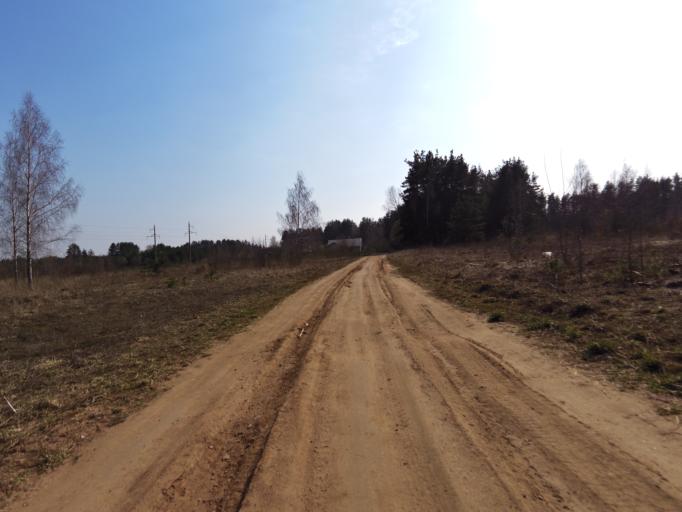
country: LT
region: Vilnius County
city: Pilaite
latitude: 54.6934
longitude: 25.1668
